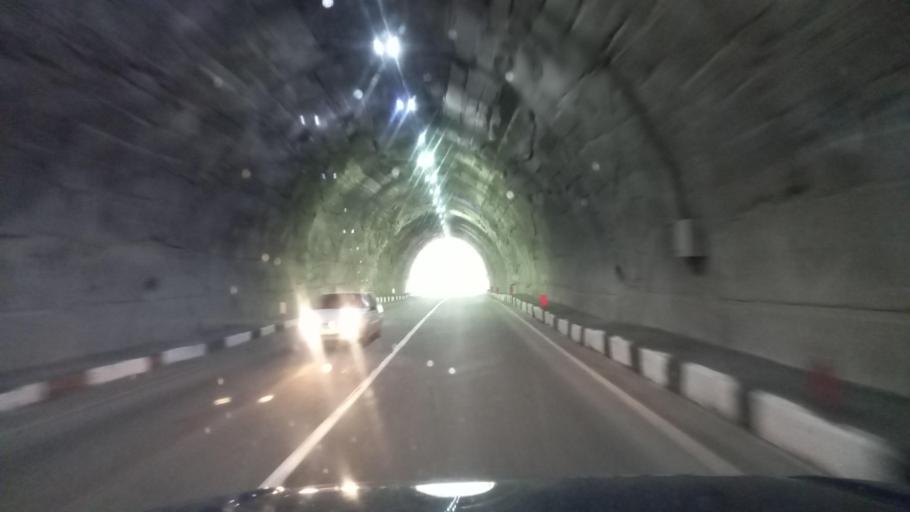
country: RU
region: North Ossetia
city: Mizur
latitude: 42.8565
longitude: 44.1038
